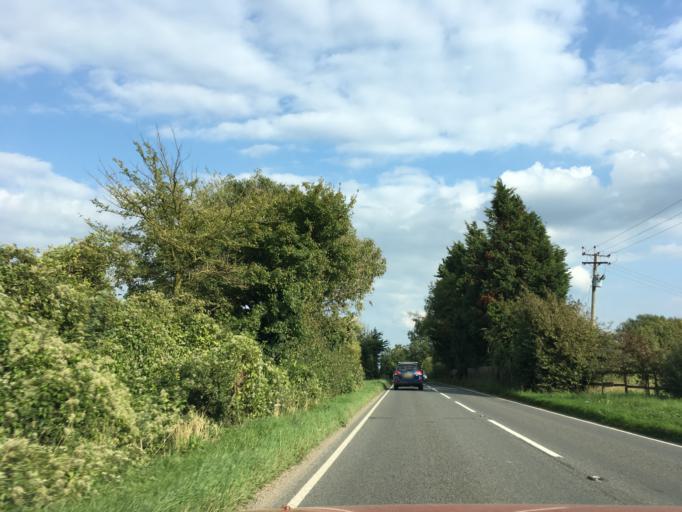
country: GB
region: England
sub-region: Gloucestershire
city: Nailsworth
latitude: 51.6474
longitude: -2.2213
